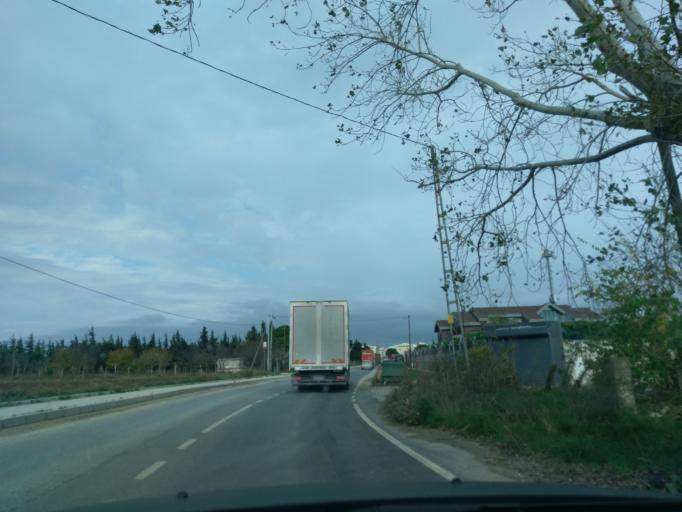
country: TR
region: Istanbul
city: Selimpasa
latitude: 41.0711
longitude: 28.3701
